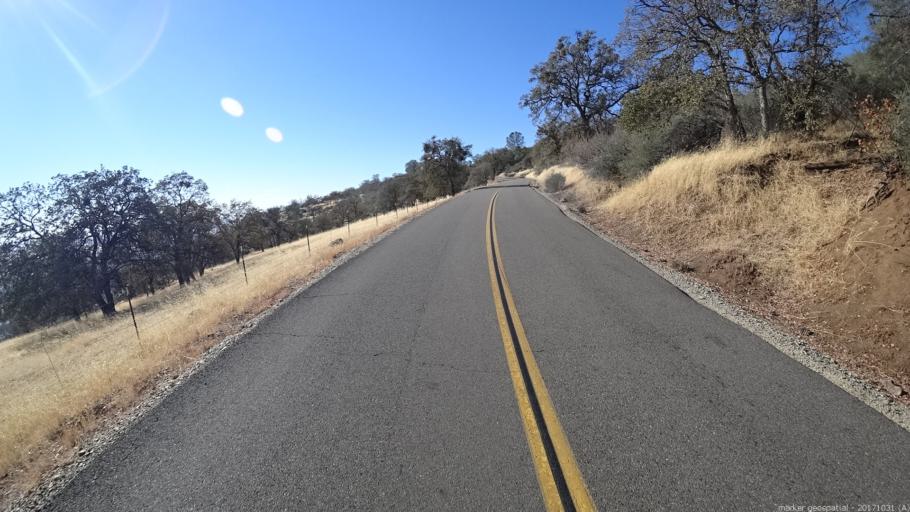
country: US
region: California
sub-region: Shasta County
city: Shingletown
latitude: 40.4452
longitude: -122.0014
